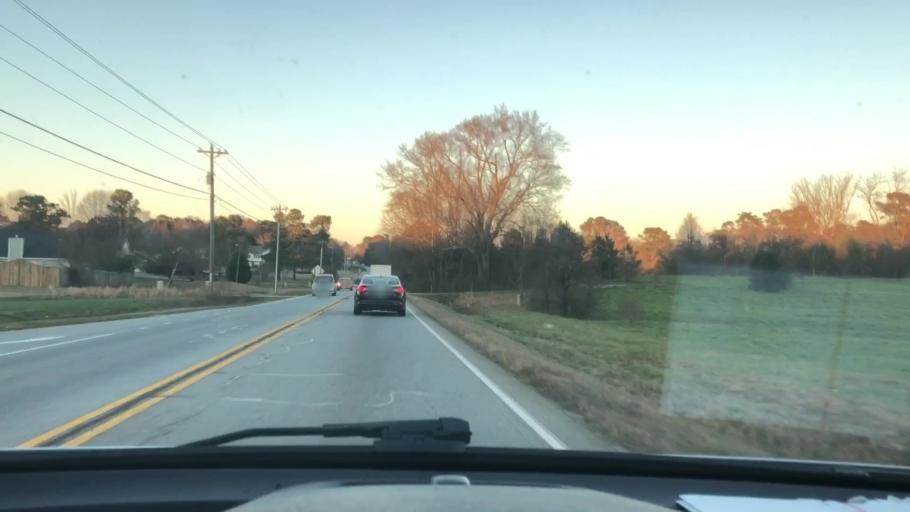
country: US
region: Georgia
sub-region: Barrow County
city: Winder
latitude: 33.9278
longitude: -83.7696
